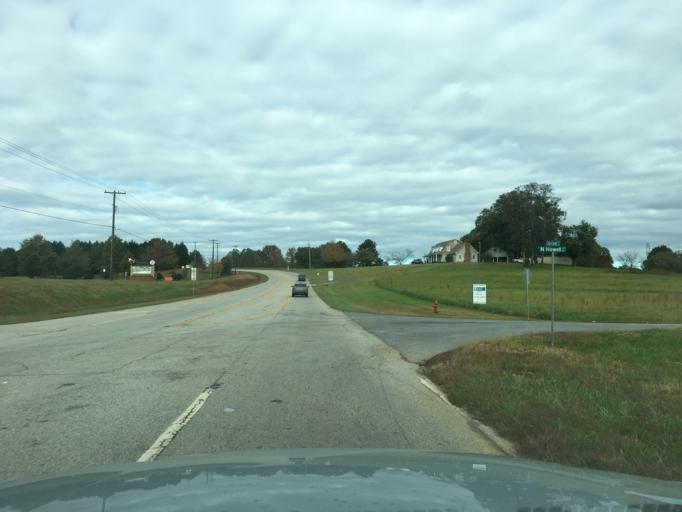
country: US
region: South Carolina
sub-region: Greenville County
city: Greer
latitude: 34.9824
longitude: -82.2295
